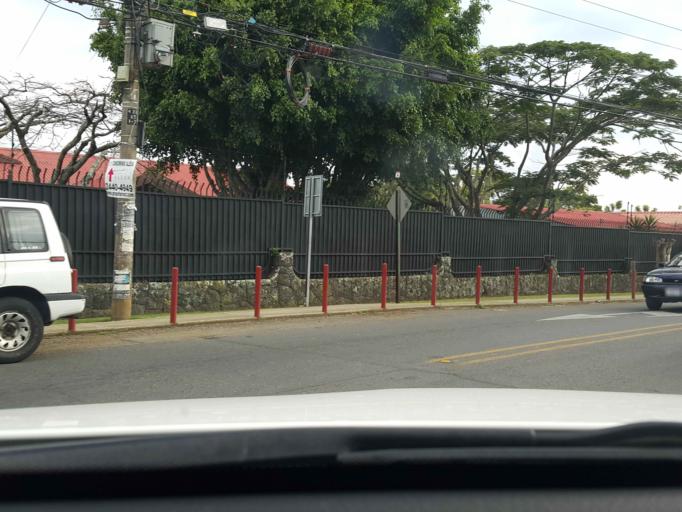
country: CR
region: Heredia
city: San Pablo
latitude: 10.0025
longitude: -84.0943
